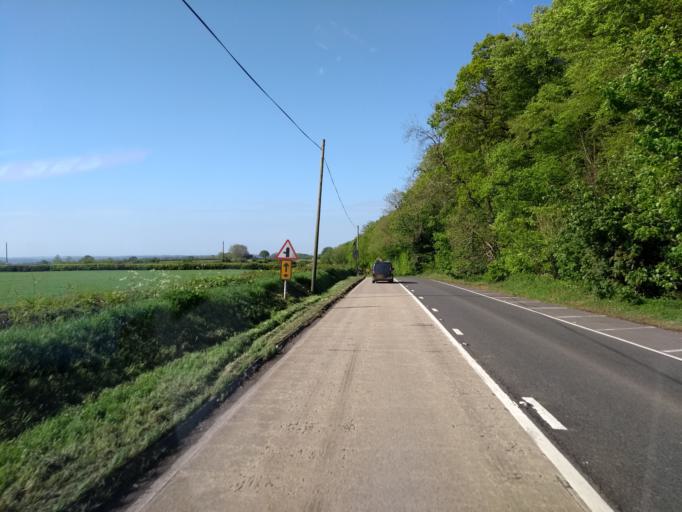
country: GB
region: England
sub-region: Devon
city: Honiton
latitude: 50.8518
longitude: -3.1242
